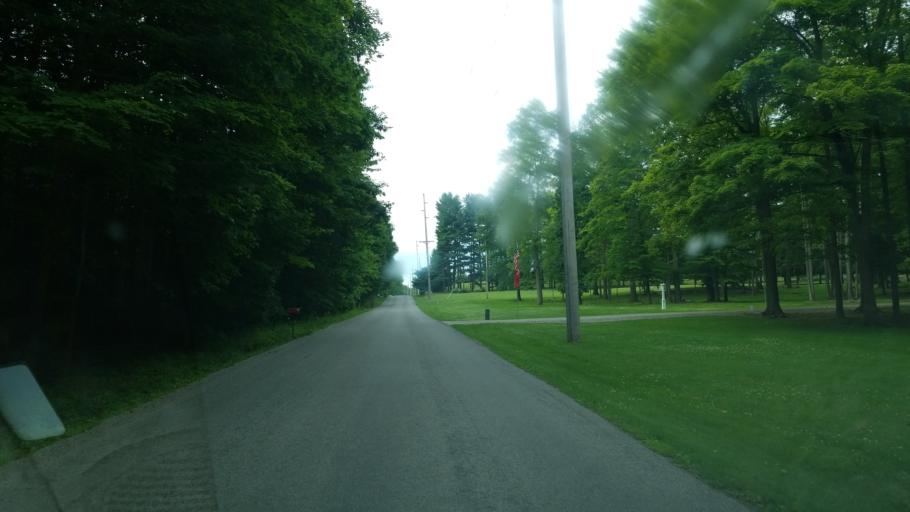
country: US
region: Ohio
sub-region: Ashland County
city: Ashland
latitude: 40.8494
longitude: -82.2889
